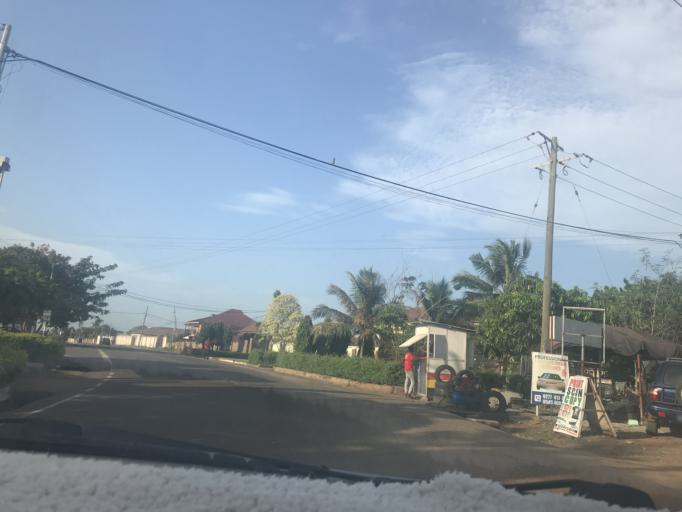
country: GH
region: Greater Accra
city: Medina Estates
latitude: 5.6689
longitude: -0.1779
